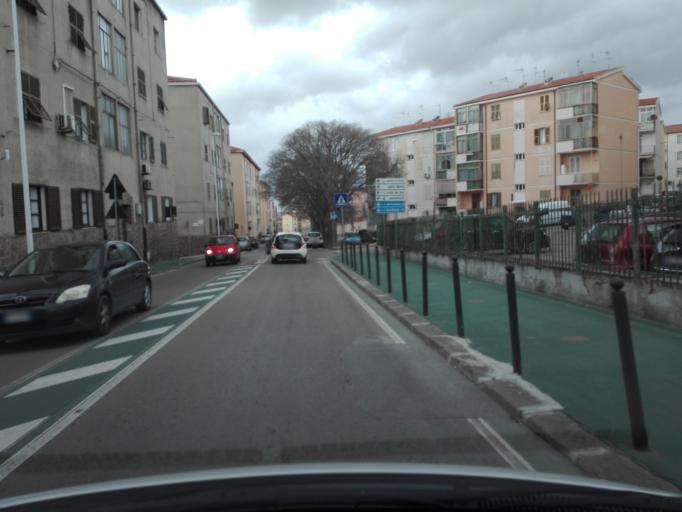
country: IT
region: Sardinia
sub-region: Provincia di Sassari
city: Sassari
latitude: 40.7361
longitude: 8.5675
